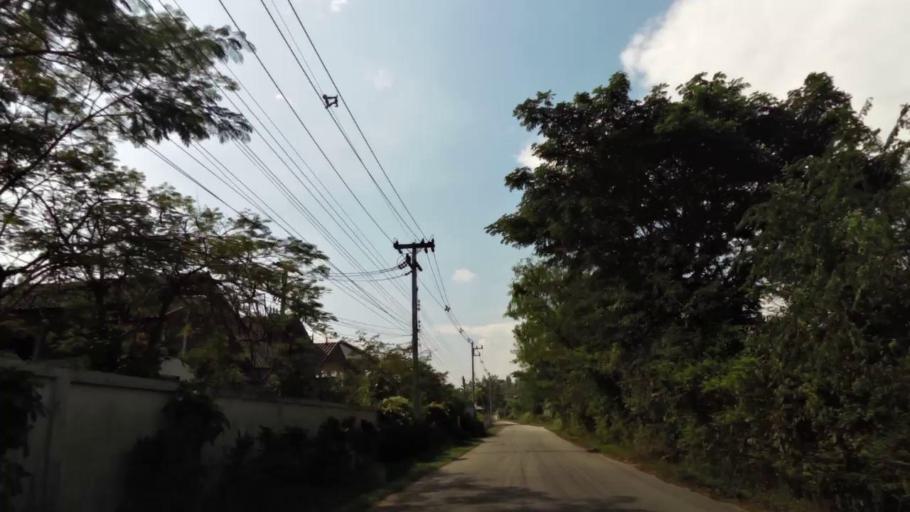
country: TH
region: Chiang Rai
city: Chiang Rai
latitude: 19.8886
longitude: 99.8145
